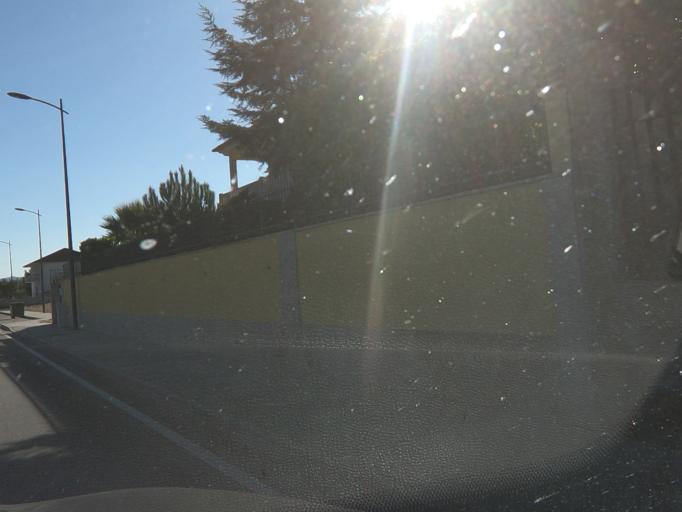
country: PT
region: Vila Real
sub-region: Valpacos
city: Valpacos
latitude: 41.5928
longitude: -7.3068
